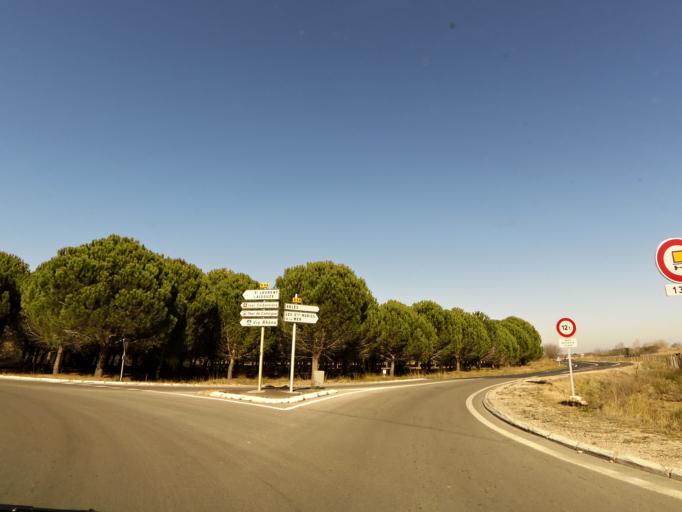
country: FR
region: Languedoc-Roussillon
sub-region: Departement du Gard
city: Aigues-Mortes
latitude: 43.5857
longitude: 4.2101
